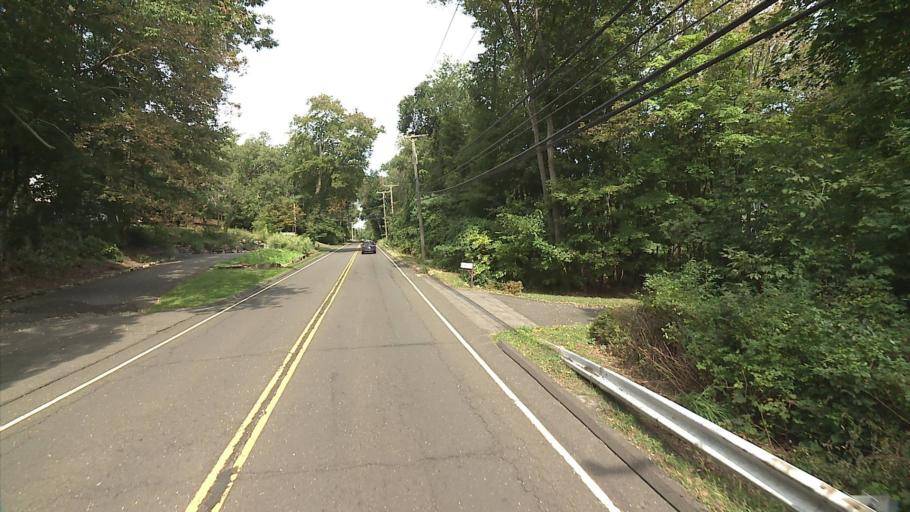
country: US
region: Connecticut
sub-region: Fairfield County
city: North Stamford
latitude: 41.1425
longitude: -73.5462
